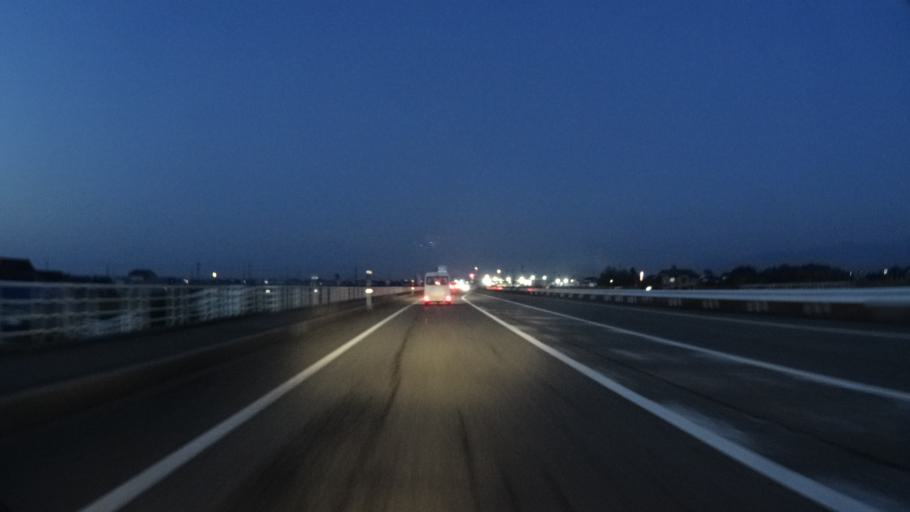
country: JP
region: Toyama
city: Nyuzen
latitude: 36.9109
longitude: 137.4563
